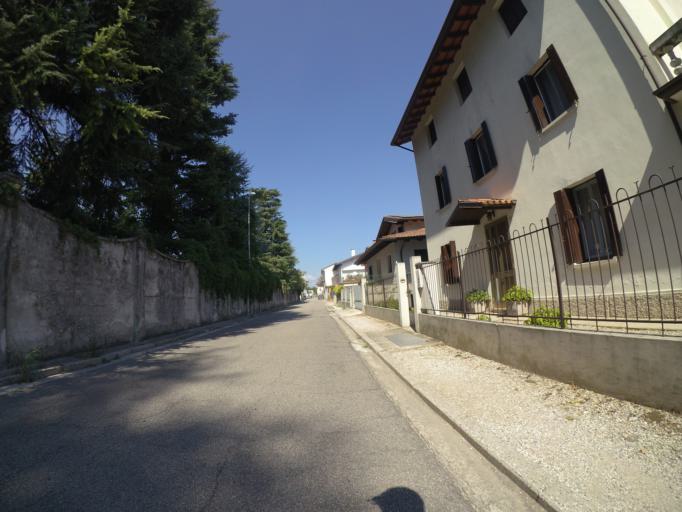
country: IT
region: Friuli Venezia Giulia
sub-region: Provincia di Udine
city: Codroipo
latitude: 45.9647
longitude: 12.9824
